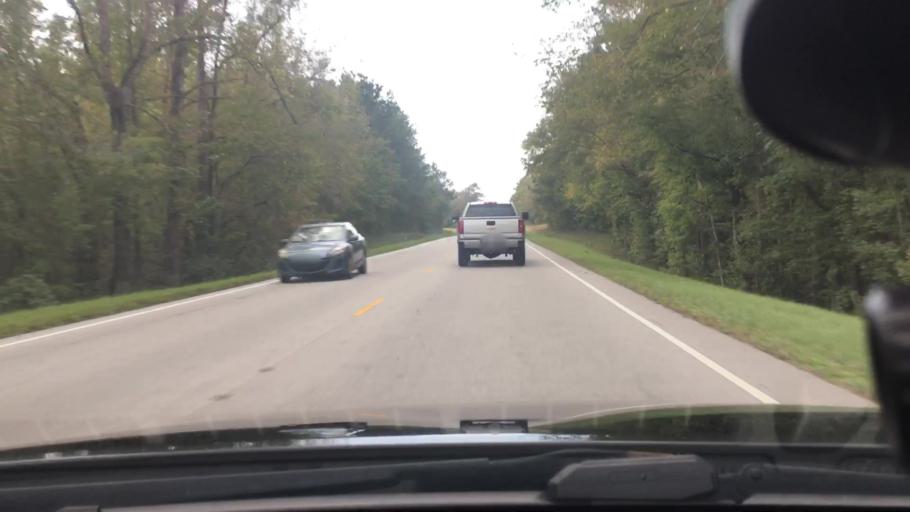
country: US
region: North Carolina
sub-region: Craven County
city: Vanceboro
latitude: 35.3034
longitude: -77.1339
